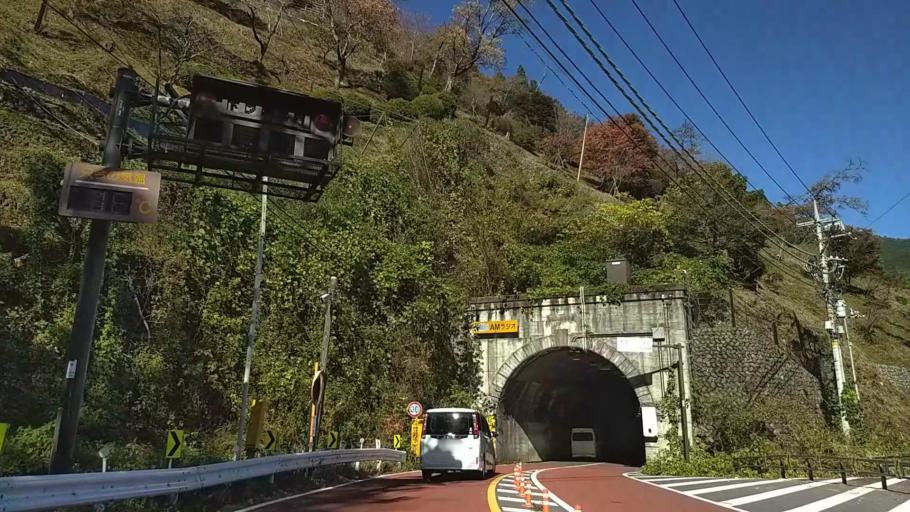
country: JP
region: Tokyo
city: Itsukaichi
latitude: 35.7900
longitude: 139.0424
